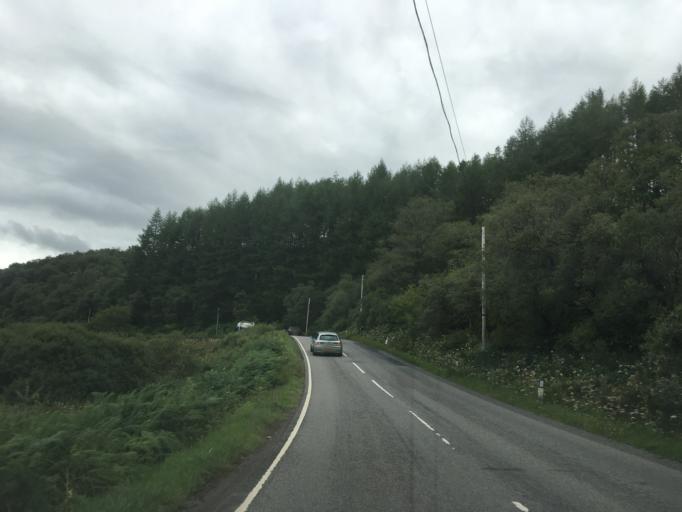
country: GB
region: Scotland
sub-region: Argyll and Bute
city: Oban
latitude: 56.3053
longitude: -5.4690
